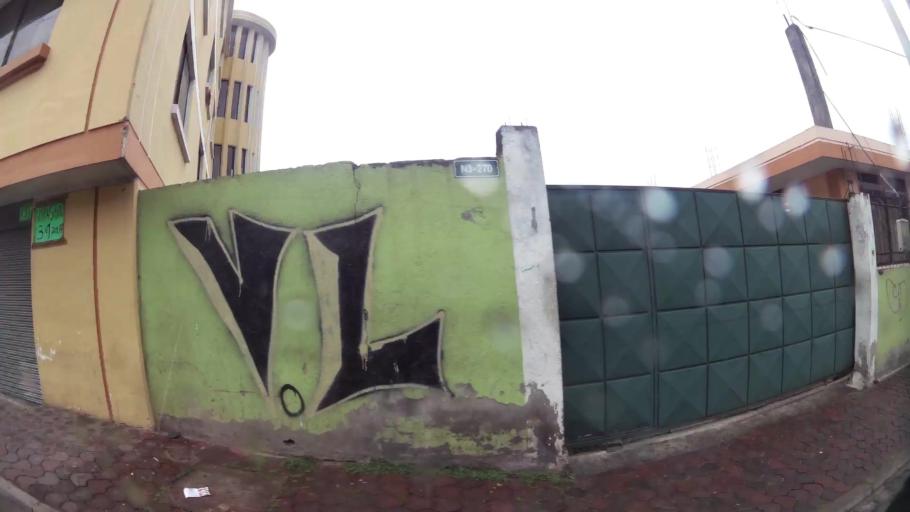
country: EC
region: Pichincha
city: Sangolqui
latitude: -0.2866
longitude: -78.4404
